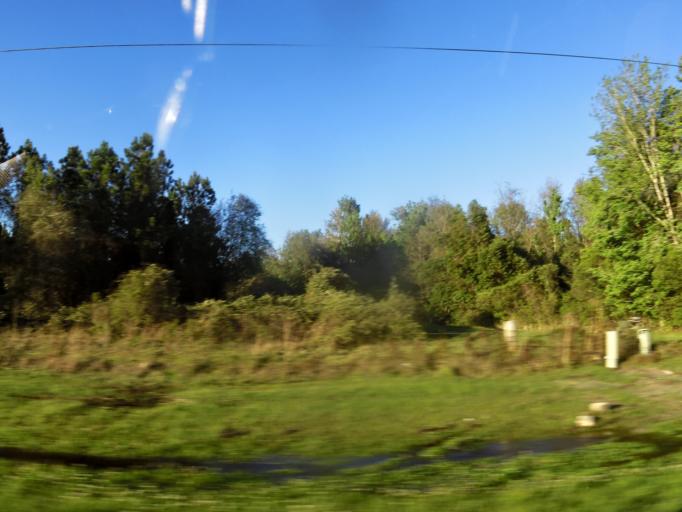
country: US
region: Florida
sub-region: Clay County
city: Keystone Heights
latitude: 29.8466
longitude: -82.0803
